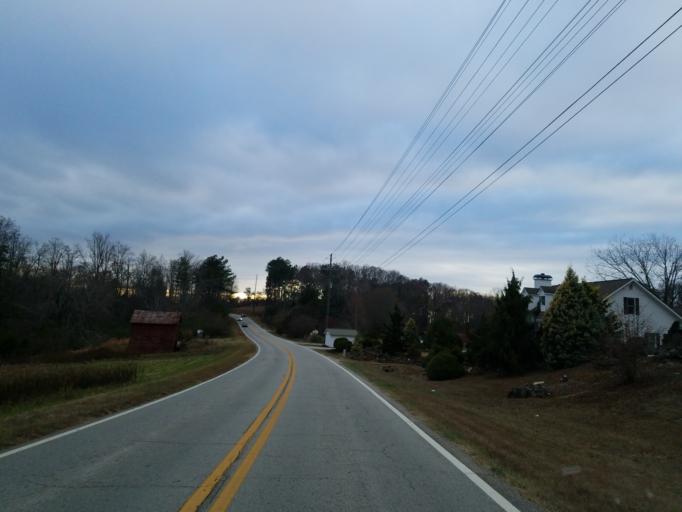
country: US
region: Georgia
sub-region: Dawson County
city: Dawsonville
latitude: 34.3761
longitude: -84.0320
